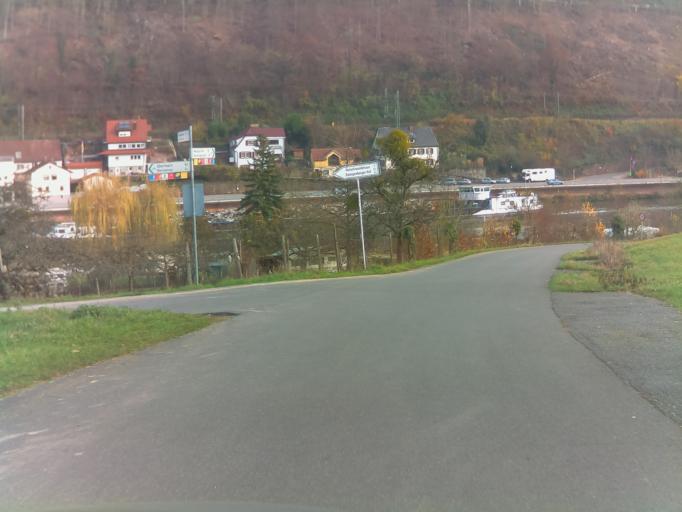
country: DE
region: Baden-Wuerttemberg
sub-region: Karlsruhe Region
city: Zwingenberg
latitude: 49.4178
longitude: 9.0363
